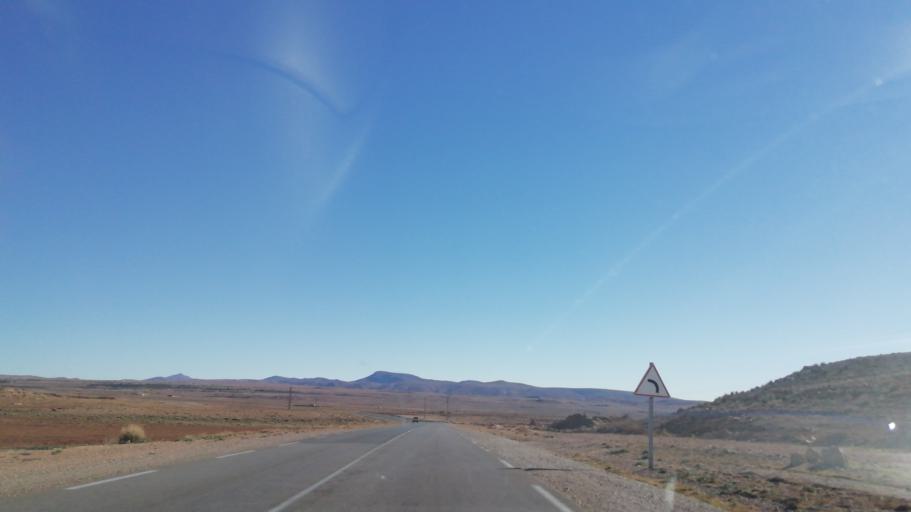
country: DZ
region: El Bayadh
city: El Bayadh
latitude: 33.6037
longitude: 1.2859
